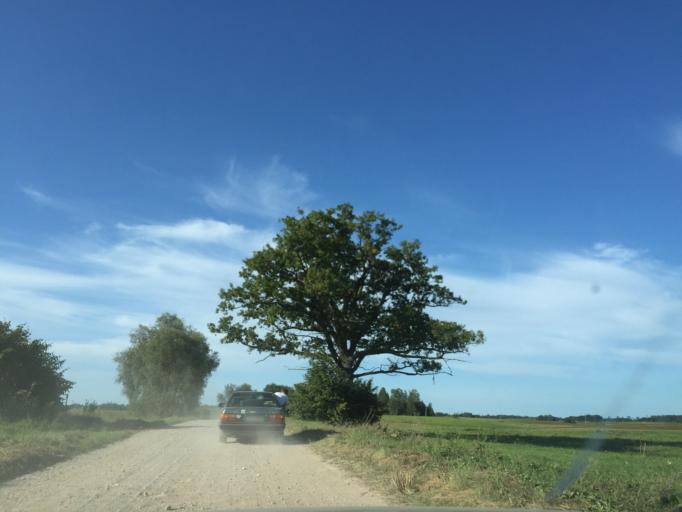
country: LT
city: Zarasai
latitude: 55.8008
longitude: 25.9485
